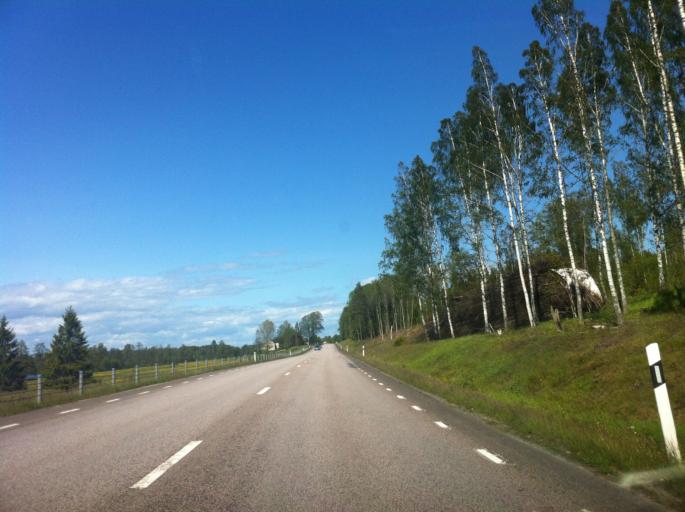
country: SE
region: Vaestra Goetaland
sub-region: Gullspangs Kommun
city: Gullspang
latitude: 59.0021
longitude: 14.1007
